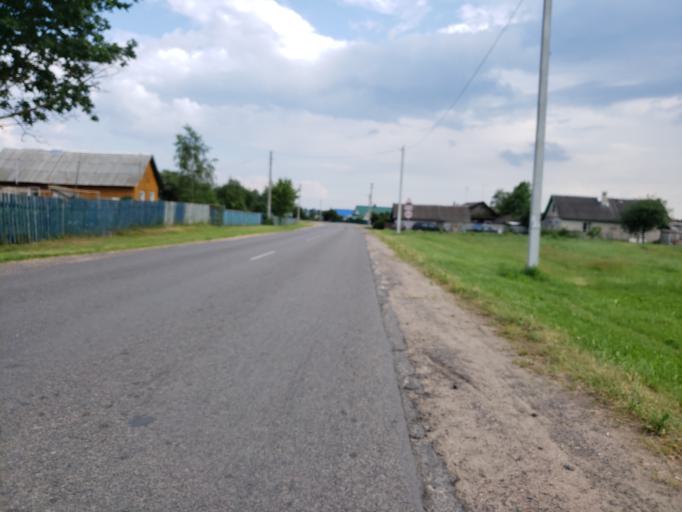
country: BY
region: Minsk
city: Chervyen'
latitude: 53.7315
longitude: 28.3881
